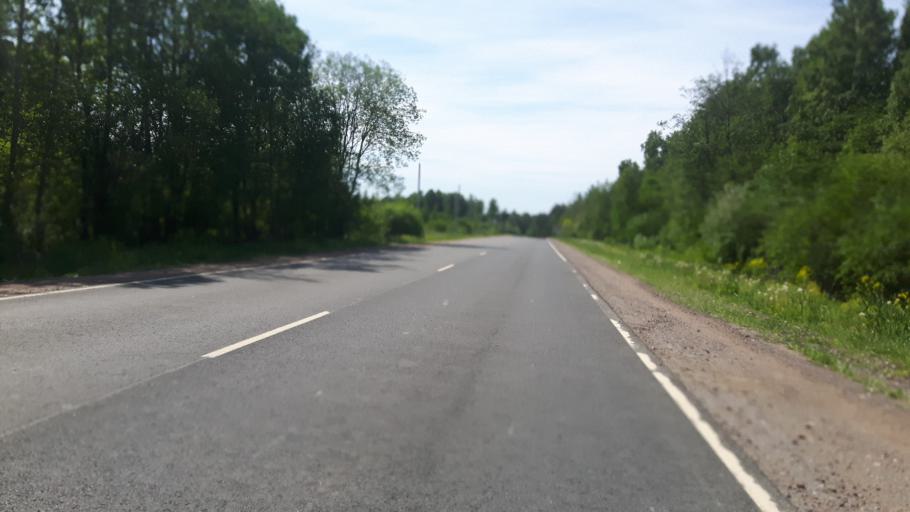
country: RU
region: Leningrad
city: Vistino
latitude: 59.6756
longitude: 28.4516
